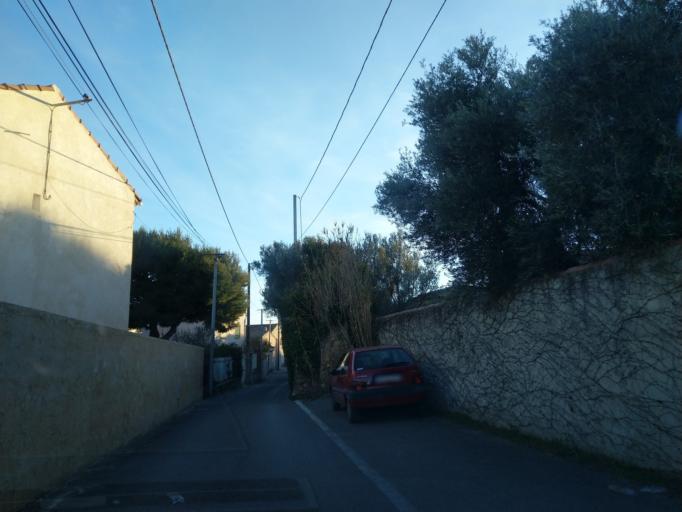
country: FR
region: Provence-Alpes-Cote d'Azur
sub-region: Departement des Bouches-du-Rhone
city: Plan-de-Cuques
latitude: 43.3420
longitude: 5.4511
